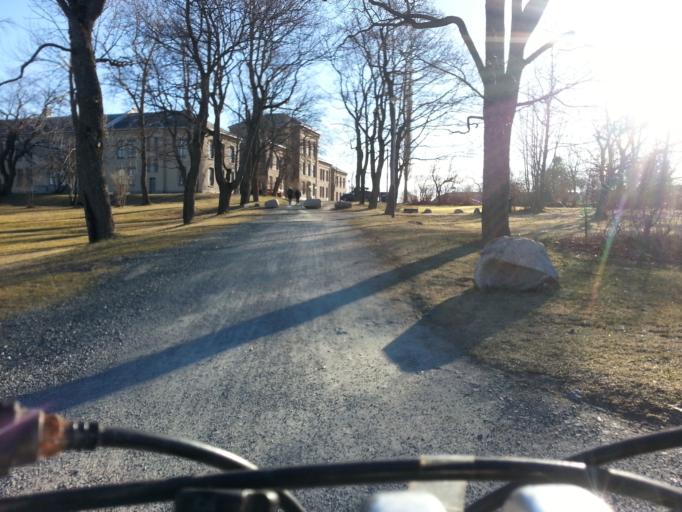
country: NO
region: Sor-Trondelag
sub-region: Trondheim
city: Trondheim
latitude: 63.4388
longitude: 10.4812
